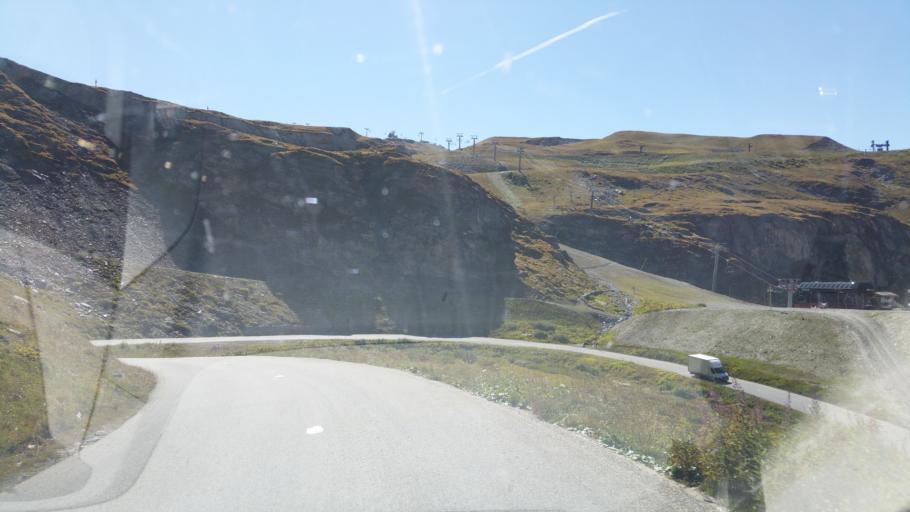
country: FR
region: Rhone-Alpes
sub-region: Departement de la Savoie
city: Val-d'Isere
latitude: 45.4324
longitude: 7.0031
